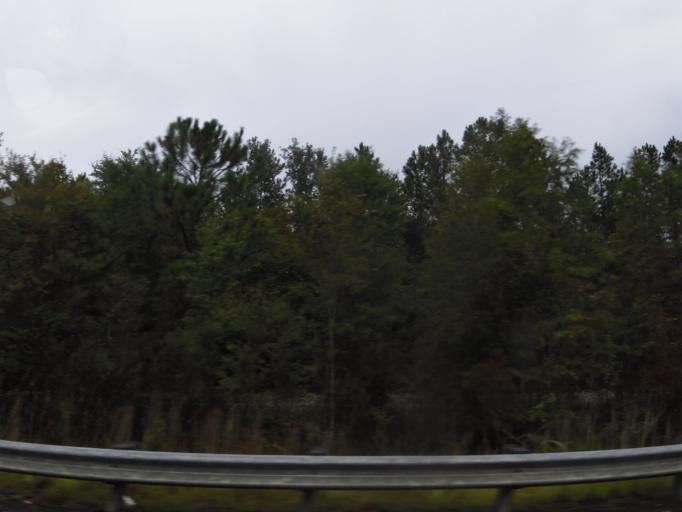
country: US
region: Georgia
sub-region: Wayne County
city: Jesup
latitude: 31.5214
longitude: -81.7791
